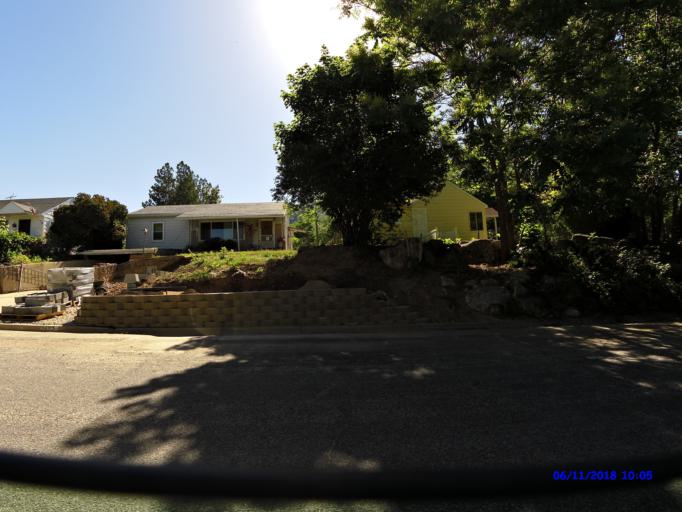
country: US
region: Utah
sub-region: Weber County
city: Ogden
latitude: 41.2269
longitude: -111.9453
